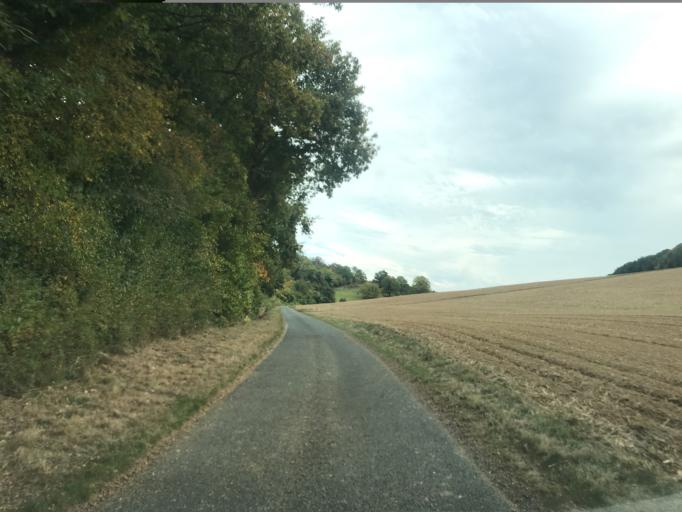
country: FR
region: Haute-Normandie
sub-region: Departement de l'Eure
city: Heudreville-sur-Eure
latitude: 49.0938
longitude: 1.2239
